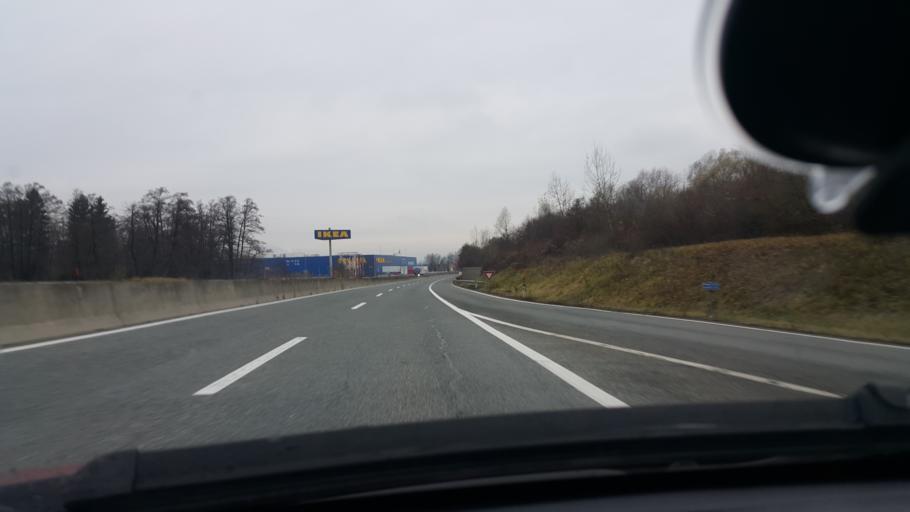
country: AT
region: Carinthia
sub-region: Politischer Bezirk Klagenfurt Land
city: Ebenthal
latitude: 46.6428
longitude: 14.3740
